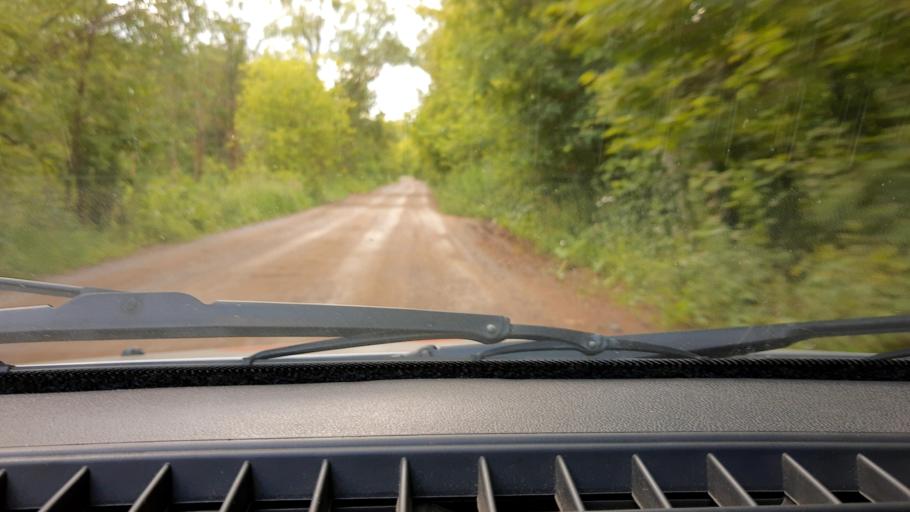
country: RU
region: Bashkortostan
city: Ufa
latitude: 54.6739
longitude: 56.0652
